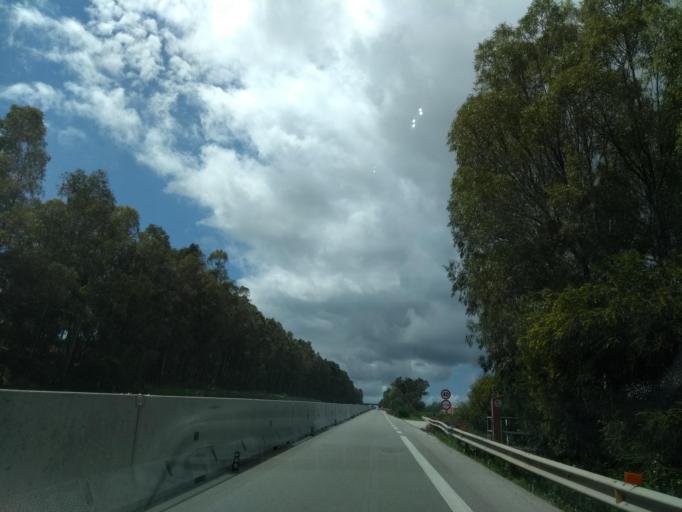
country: IT
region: Sicily
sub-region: Trapani
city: Calatafimi
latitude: 37.9478
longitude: 12.8051
